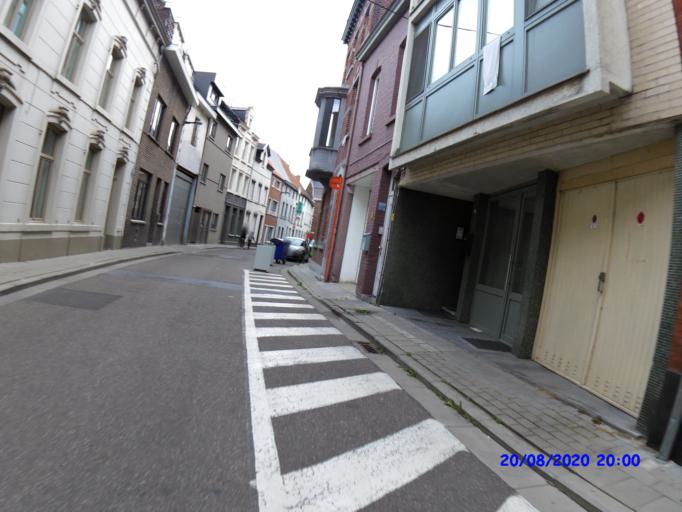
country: BE
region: Flanders
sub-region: Provincie Limburg
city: Sint-Truiden
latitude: 50.8109
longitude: 5.1802
